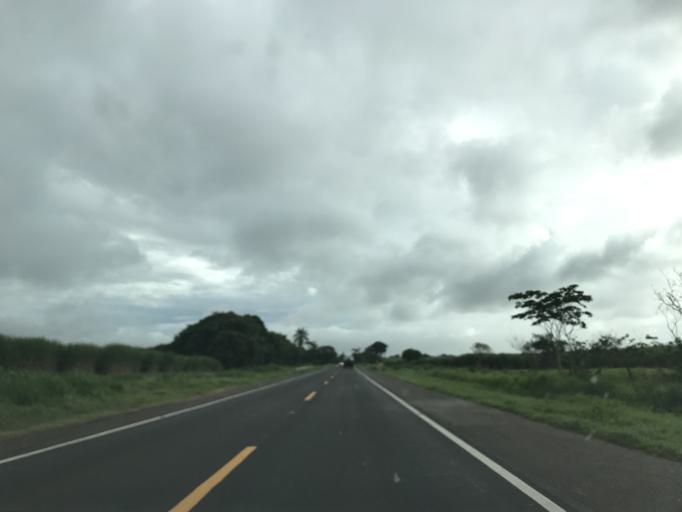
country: BR
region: Sao Paulo
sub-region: Penapolis
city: Penapolis
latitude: -21.4655
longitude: -50.1814
